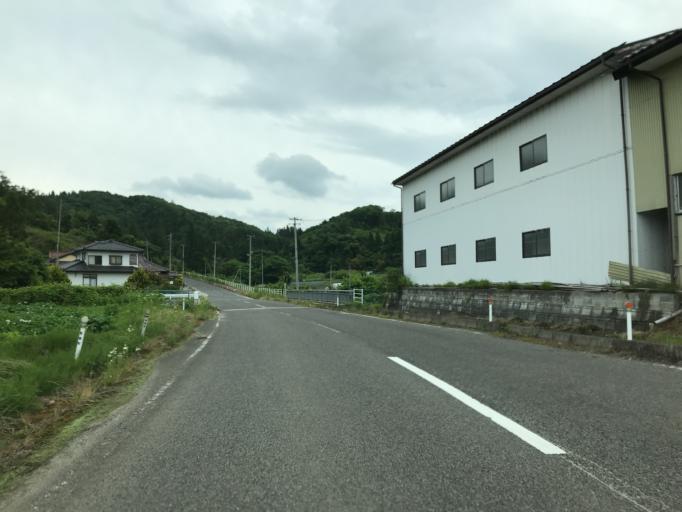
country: JP
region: Fukushima
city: Funehikimachi-funehiki
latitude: 37.4140
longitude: 140.6529
